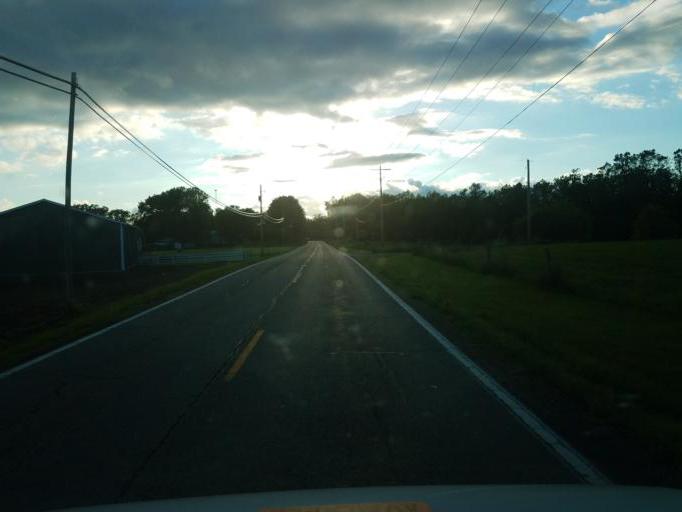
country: US
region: Ohio
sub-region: Knox County
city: Mount Vernon
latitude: 40.4010
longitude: -82.5540
